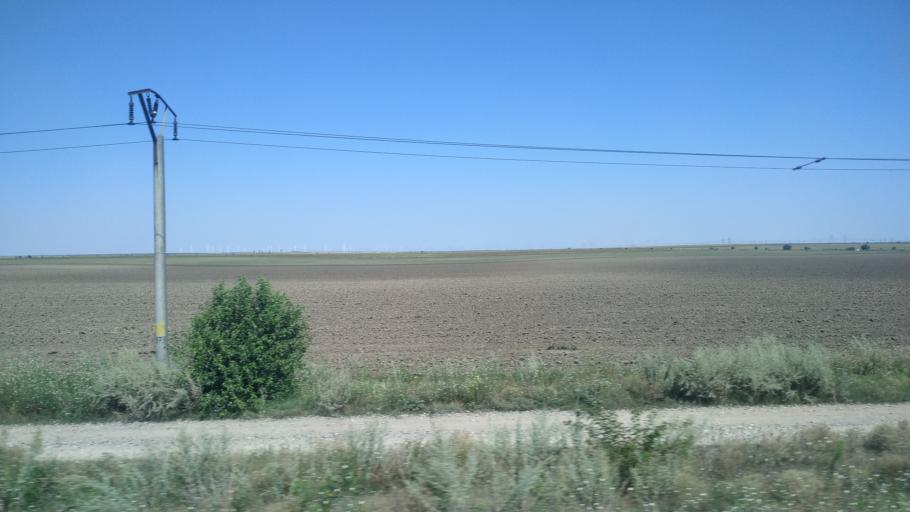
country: RO
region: Ialomita
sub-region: Municipiul Fetesti
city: Fetesti-Gara
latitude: 44.4180
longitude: 27.7894
